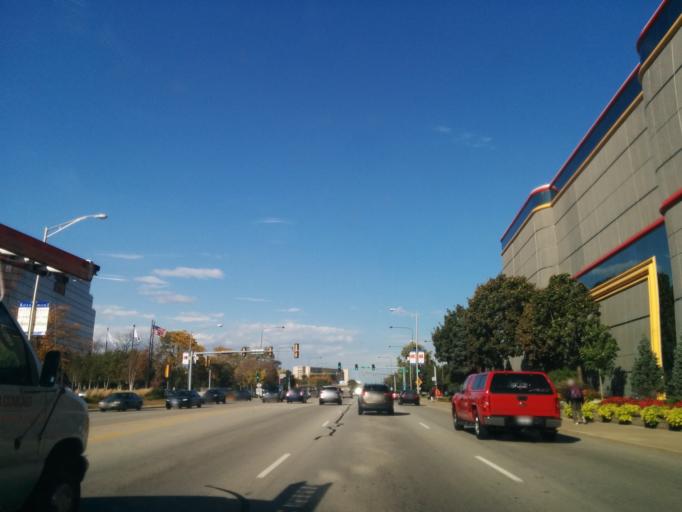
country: US
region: Illinois
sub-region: Cook County
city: Schiller Park
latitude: 41.9797
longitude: -87.8621
